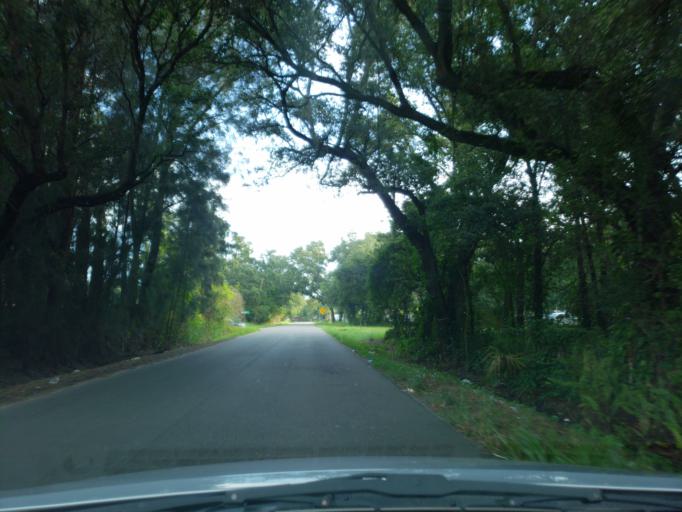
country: US
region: Florida
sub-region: Hillsborough County
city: Palm River-Clair Mel
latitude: 27.9296
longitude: -82.3606
